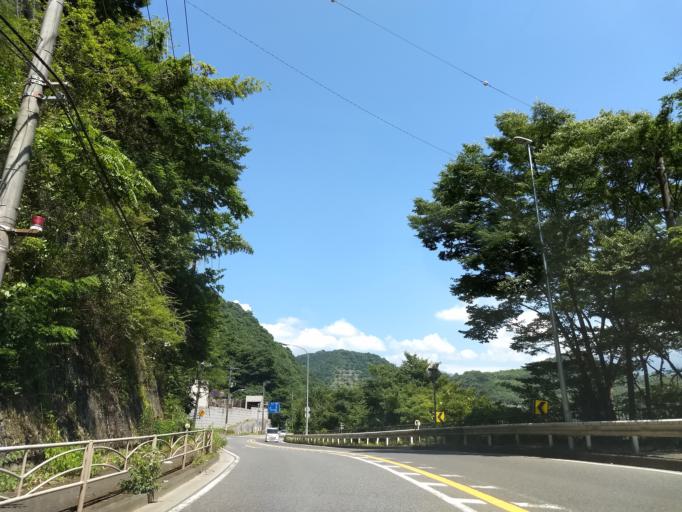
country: JP
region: Kanagawa
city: Hadano
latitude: 35.3593
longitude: 139.1592
